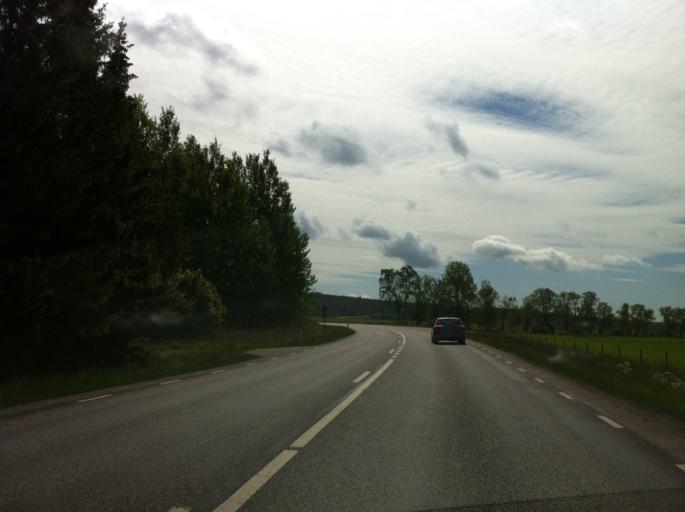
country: SE
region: Vaermland
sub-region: Saffle Kommun
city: Saeffle
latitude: 59.2168
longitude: 13.0137
